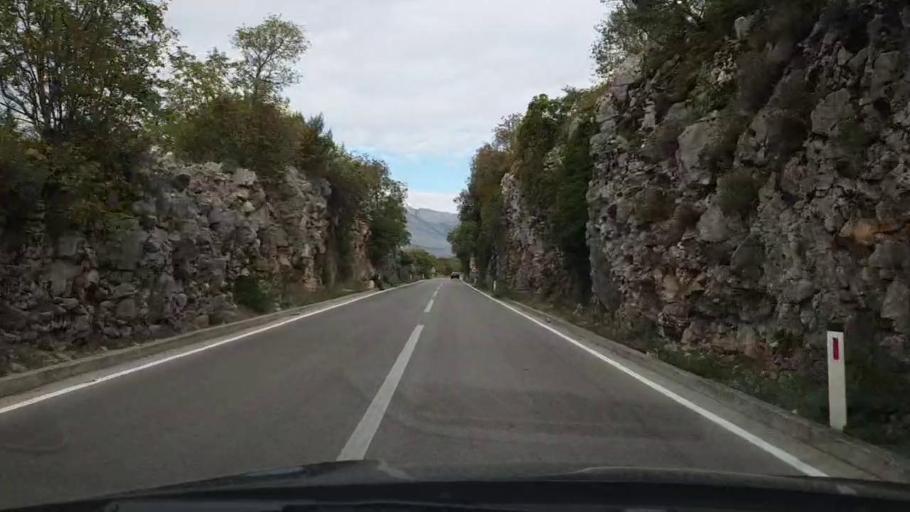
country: BA
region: Republika Srpska
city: Trebinje
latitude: 42.6818
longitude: 18.3020
